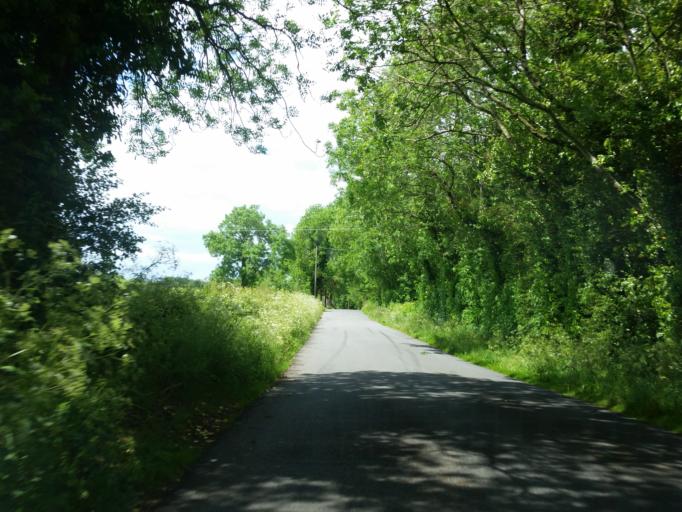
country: GB
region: Northern Ireland
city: Fivemiletown
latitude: 54.3728
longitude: -7.2993
